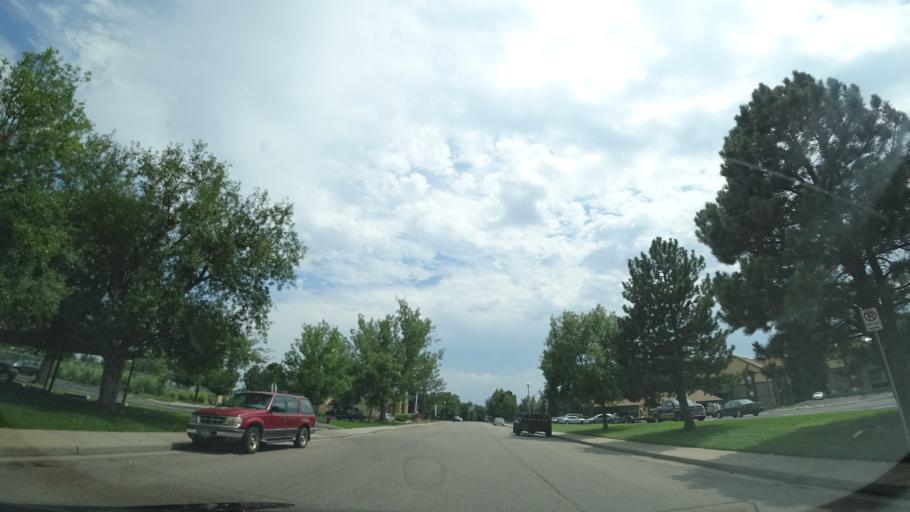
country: US
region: Colorado
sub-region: Jefferson County
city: Lakewood
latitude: 39.7042
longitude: -105.0737
